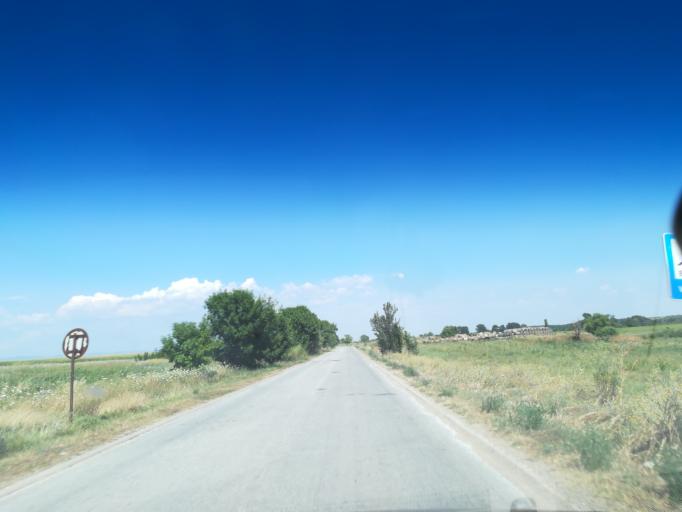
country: BG
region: Plovdiv
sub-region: Obshtina Sadovo
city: Sadovo
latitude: 42.0342
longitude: 25.1209
